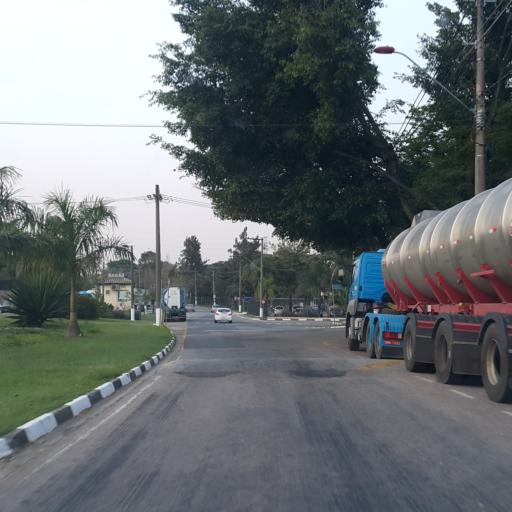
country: BR
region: Sao Paulo
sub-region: Vinhedo
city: Vinhedo
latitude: -23.0652
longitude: -46.9998
